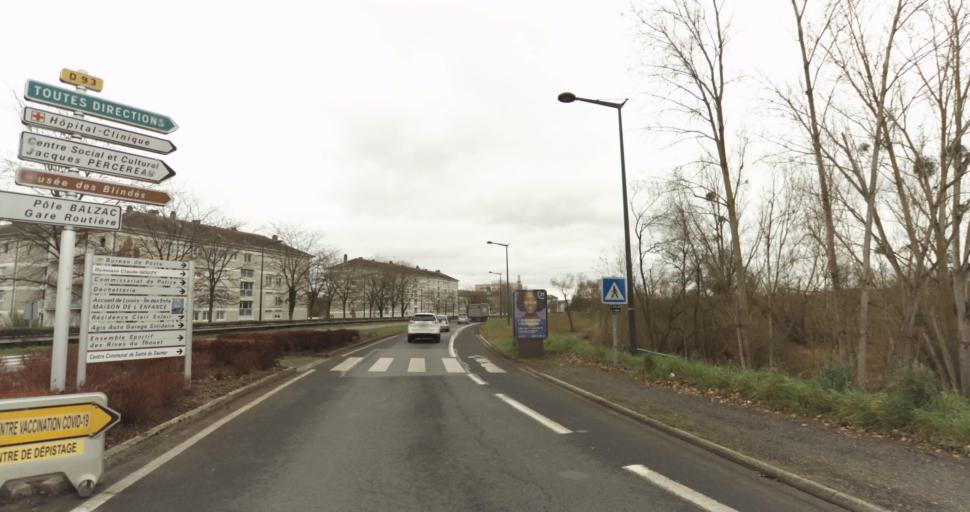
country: FR
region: Pays de la Loire
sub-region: Departement de Maine-et-Loire
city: Saumur
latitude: 47.2501
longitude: -0.0794
